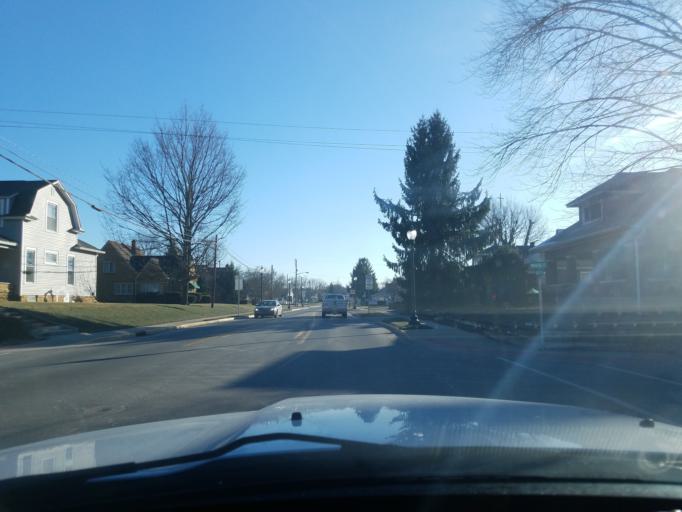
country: US
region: Indiana
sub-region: Orange County
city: Orleans
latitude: 38.6585
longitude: -86.4528
